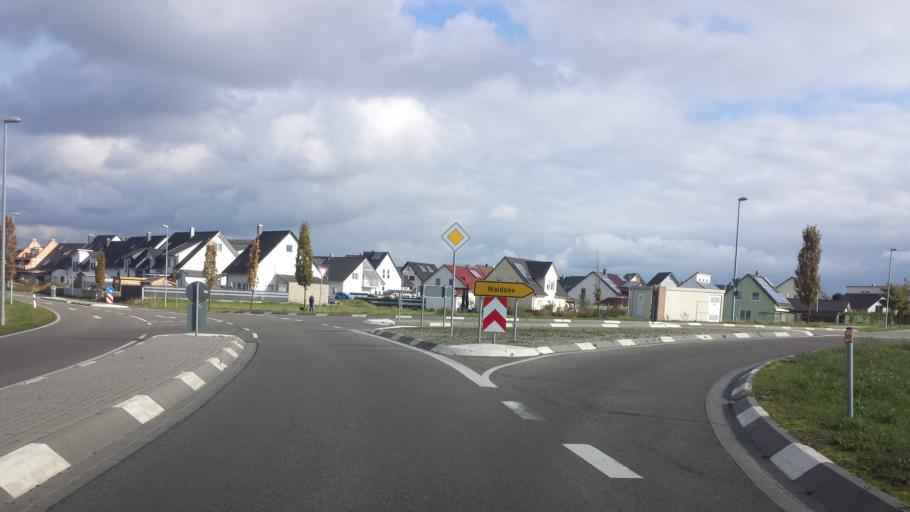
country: DE
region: Rheinland-Pfalz
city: Waldsee
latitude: 49.4000
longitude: 8.4318
